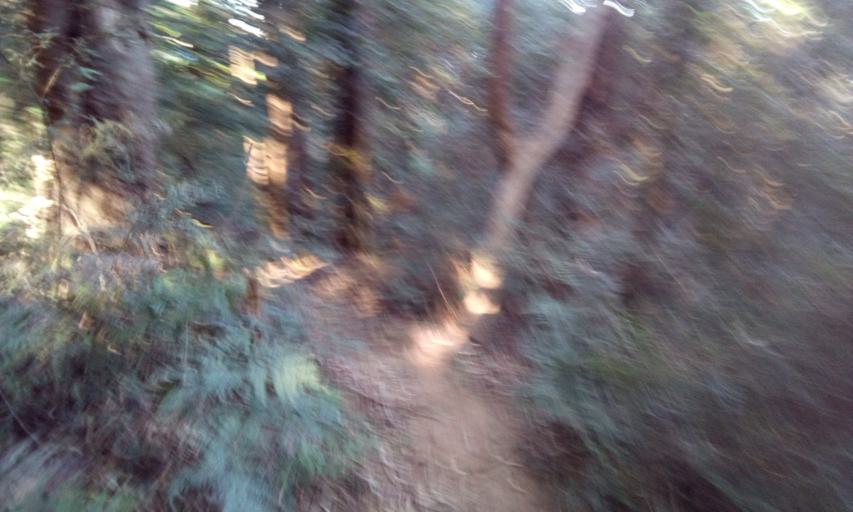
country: AU
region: New South Wales
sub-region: Wollongong
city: Mount Keira
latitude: -34.4080
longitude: 150.8557
